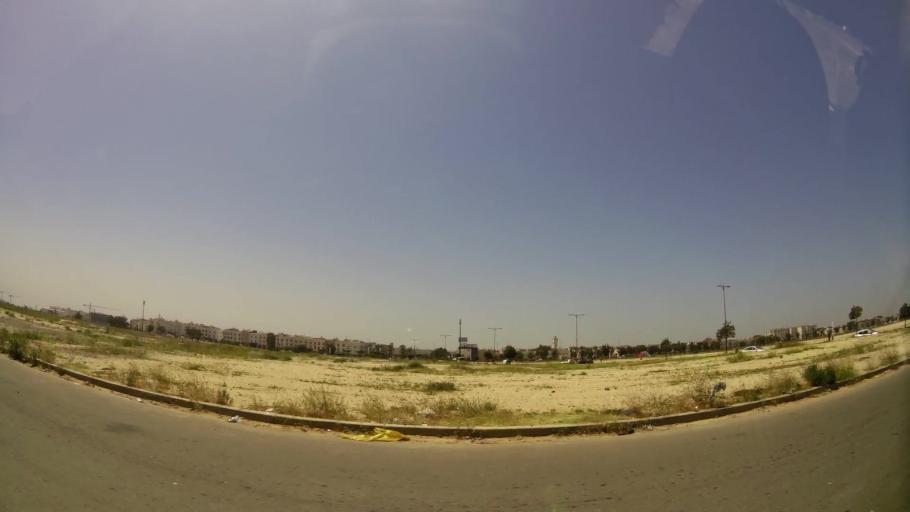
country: MA
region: Oued ed Dahab-Lagouira
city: Dakhla
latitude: 30.4262
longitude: -9.5560
